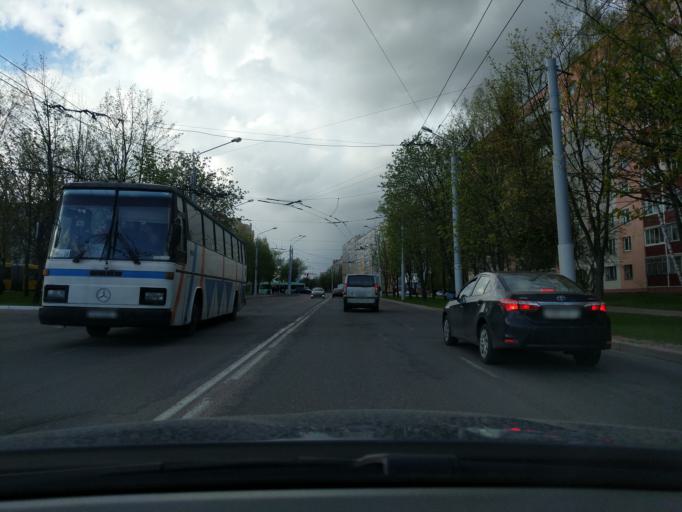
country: BY
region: Minsk
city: Novoye Medvezhino
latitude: 53.9009
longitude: 27.4816
